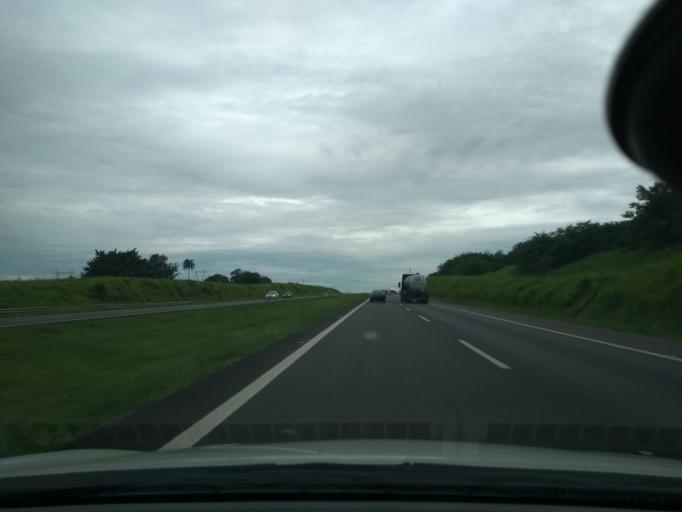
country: BR
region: Sao Paulo
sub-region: Iracemapolis
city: Iracemapolis
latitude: -22.6339
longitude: -47.4550
